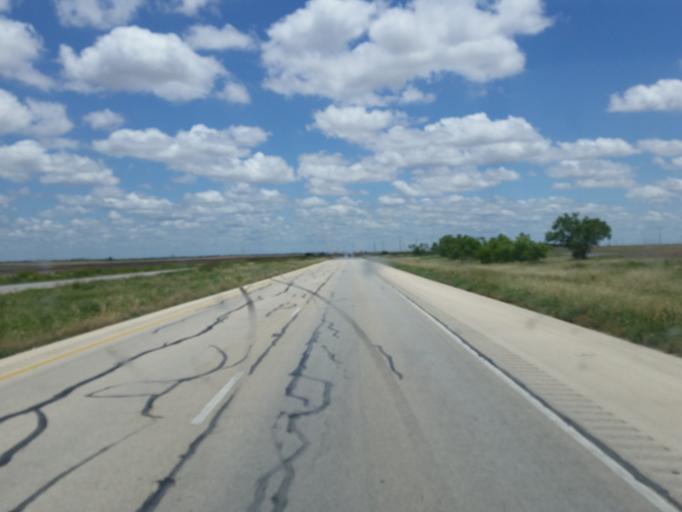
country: US
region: Texas
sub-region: Nolan County
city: Roscoe
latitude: 32.4868
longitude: -100.6277
